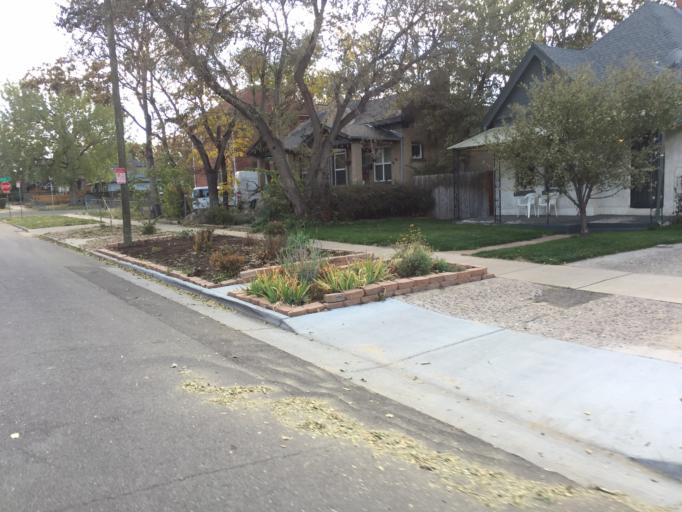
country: US
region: Colorado
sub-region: Denver County
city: Denver
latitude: 39.7589
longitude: -104.9684
